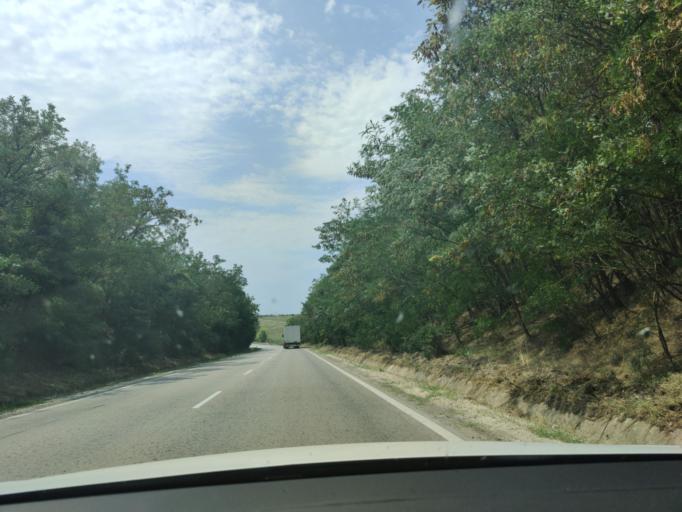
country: BG
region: Vidin
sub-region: Obshtina Vidin
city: Dunavtsi
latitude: 43.8768
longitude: 22.7871
